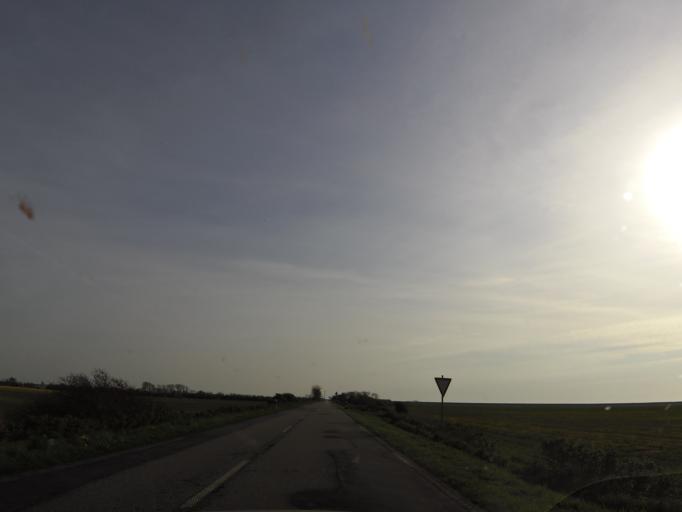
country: DE
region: Schleswig-Holstein
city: Galmsbull
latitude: 54.7497
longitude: 8.7412
